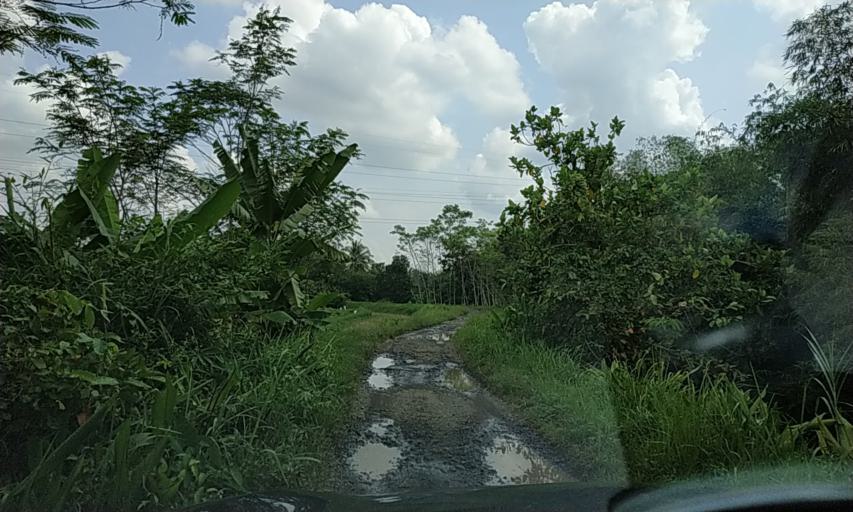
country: ID
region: Central Java
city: Bakung
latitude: -7.3377
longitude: 108.6678
